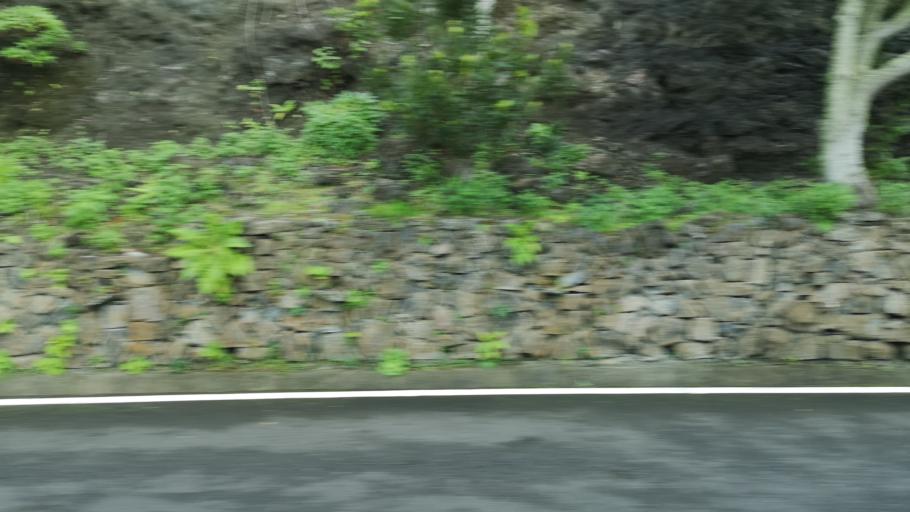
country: ES
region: Canary Islands
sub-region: Provincia de Santa Cruz de Tenerife
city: Hermigua
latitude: 28.1313
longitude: -17.2038
